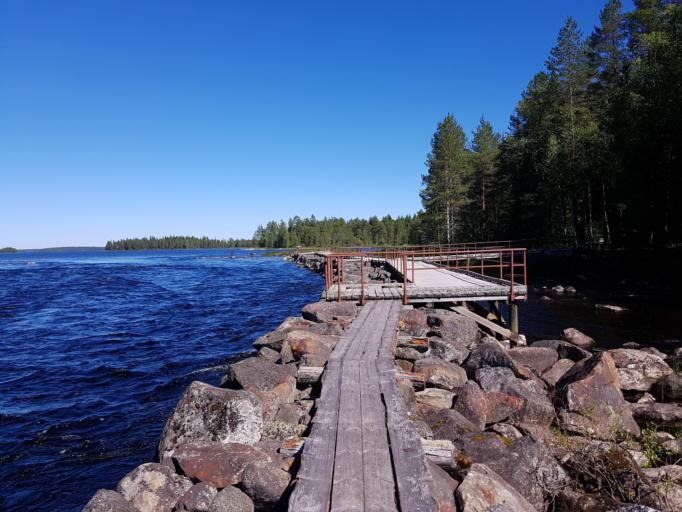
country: FI
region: Kainuu
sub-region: Kehys-Kainuu
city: Kuhmo
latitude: 64.1928
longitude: 29.5911
